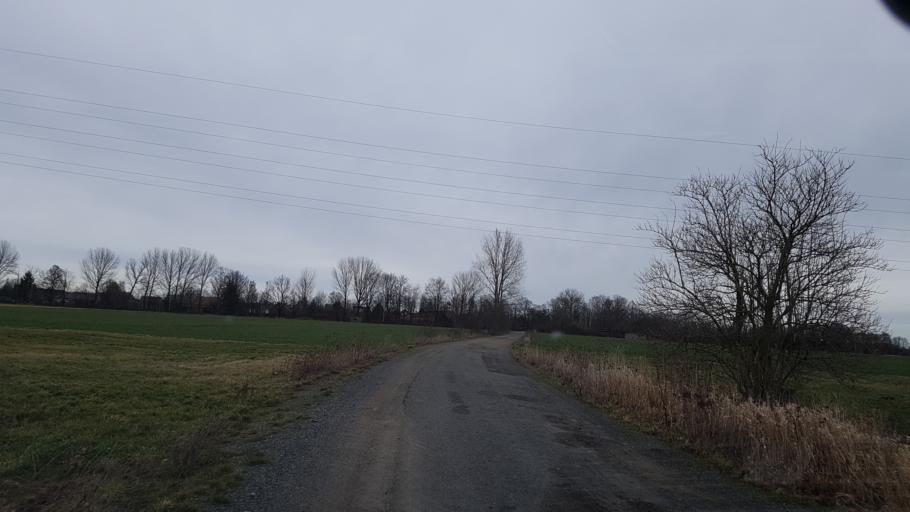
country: DE
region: Brandenburg
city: Bad Liebenwerda
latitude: 51.5078
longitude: 13.3428
